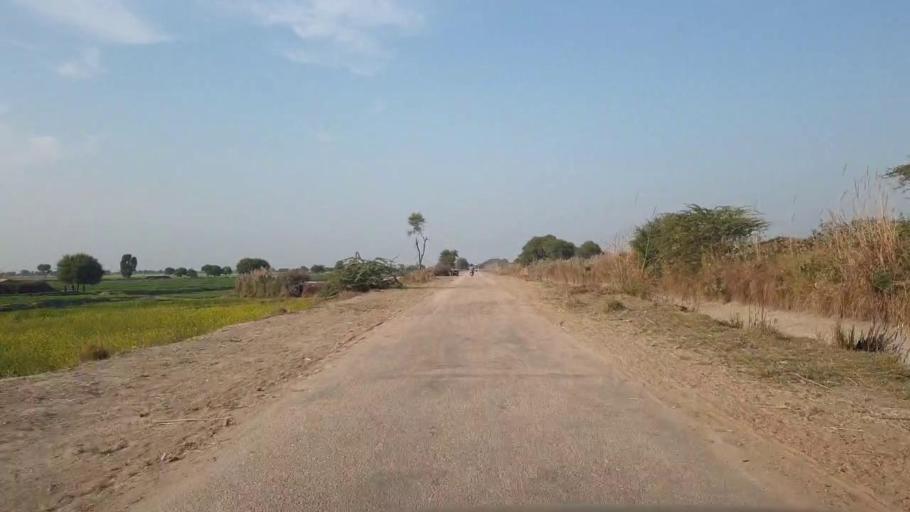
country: PK
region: Sindh
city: Shahpur Chakar
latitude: 26.1619
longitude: 68.6406
